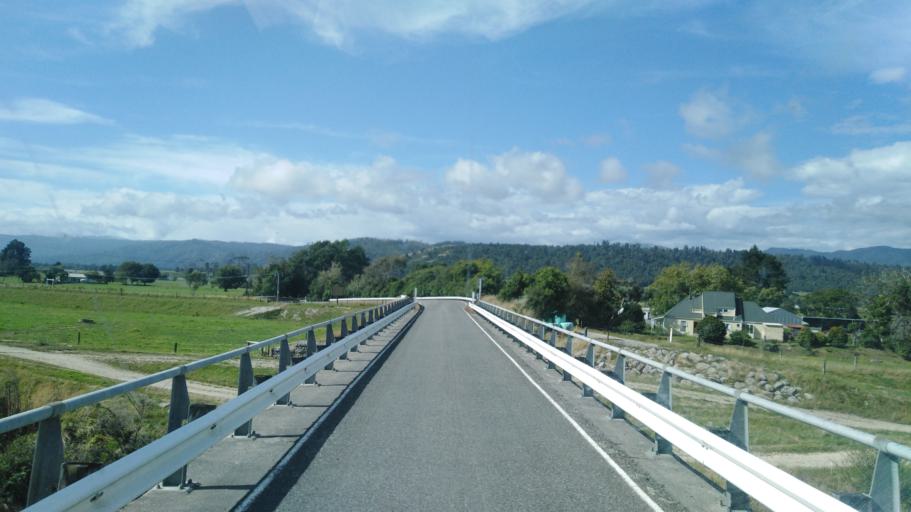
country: NZ
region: West Coast
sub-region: Buller District
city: Westport
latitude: -41.2608
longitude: 172.1314
